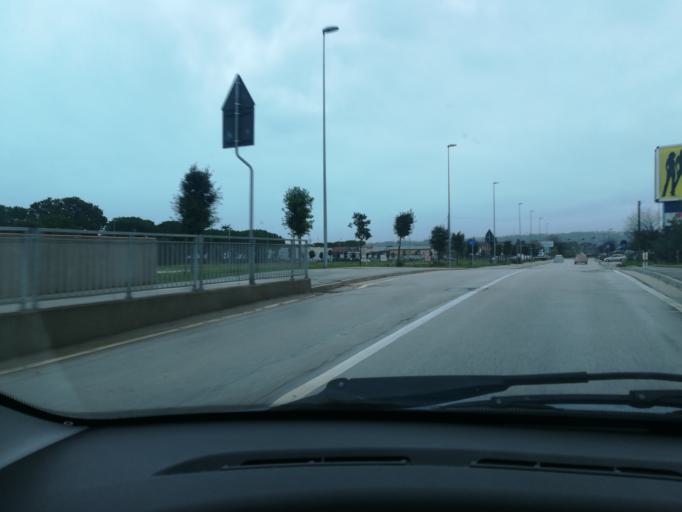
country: IT
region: The Marches
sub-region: Provincia di Macerata
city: Santa Maria Apparente
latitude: 43.2960
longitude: 13.7017
